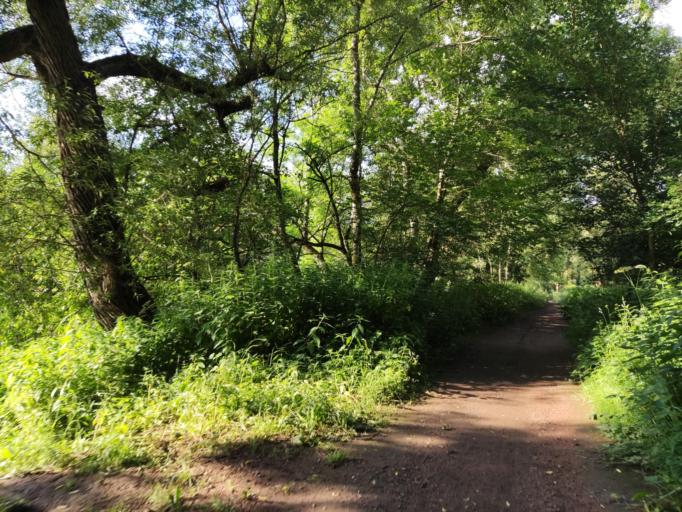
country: DE
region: Saarland
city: Rehlingen-Siersburg
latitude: 49.3642
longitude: 6.6587
